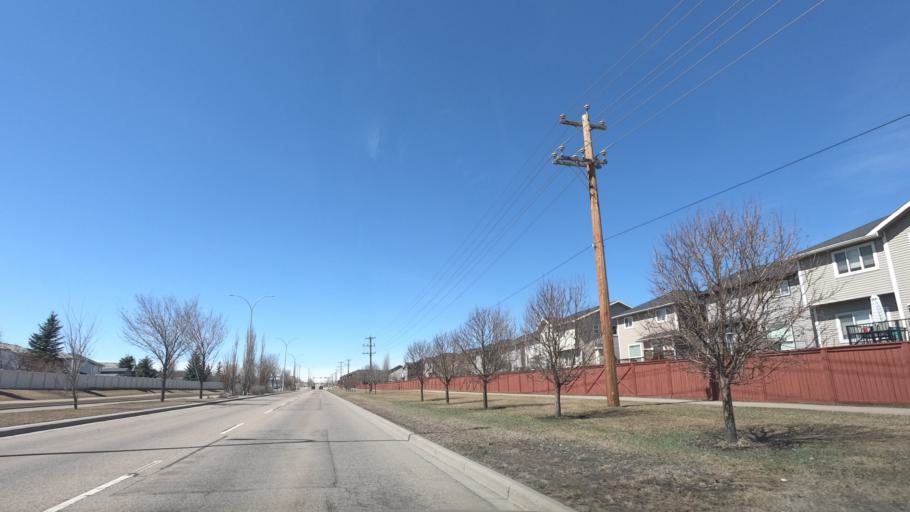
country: CA
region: Alberta
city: Airdrie
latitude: 51.3001
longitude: -114.0291
